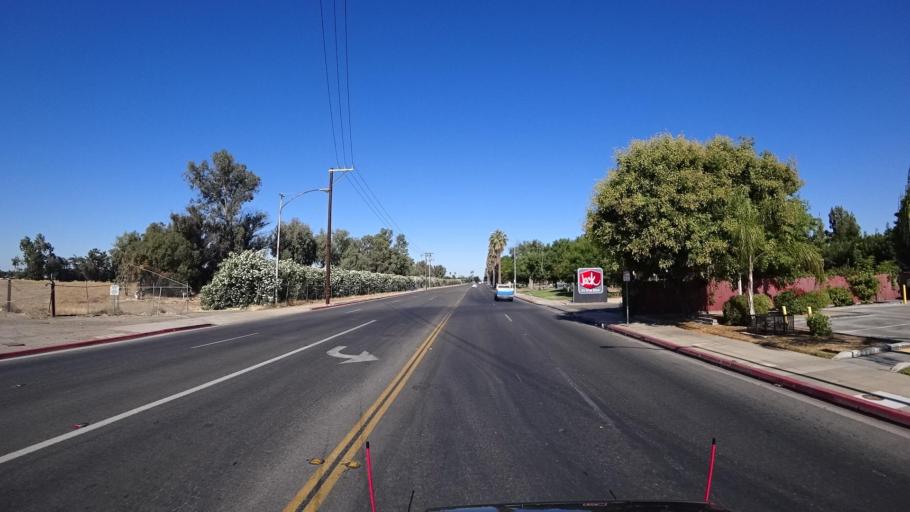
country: US
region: California
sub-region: Fresno County
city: Sunnyside
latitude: 36.7575
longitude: -119.7012
